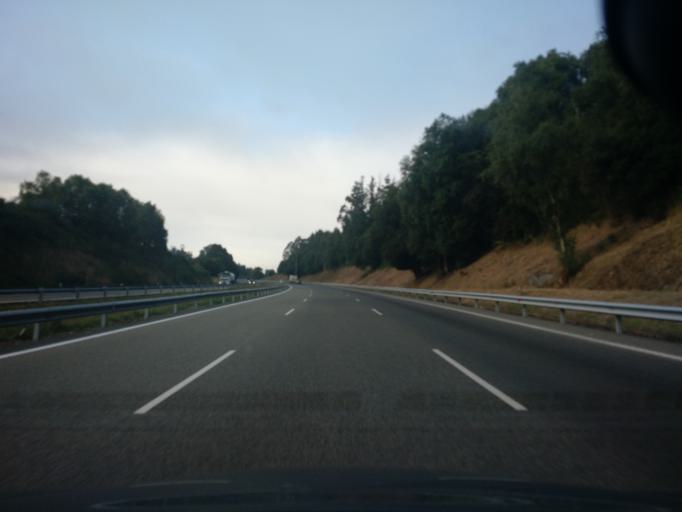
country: ES
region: Galicia
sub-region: Provincia da Coruna
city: Abegondo
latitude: 43.1875
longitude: -8.3112
